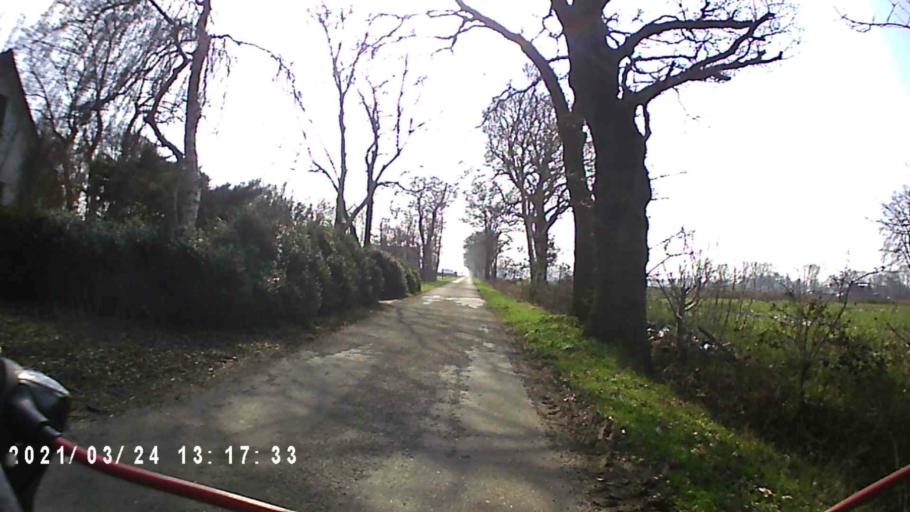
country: NL
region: Groningen
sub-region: Gemeente Leek
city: Leek
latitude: 53.1092
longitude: 6.2923
